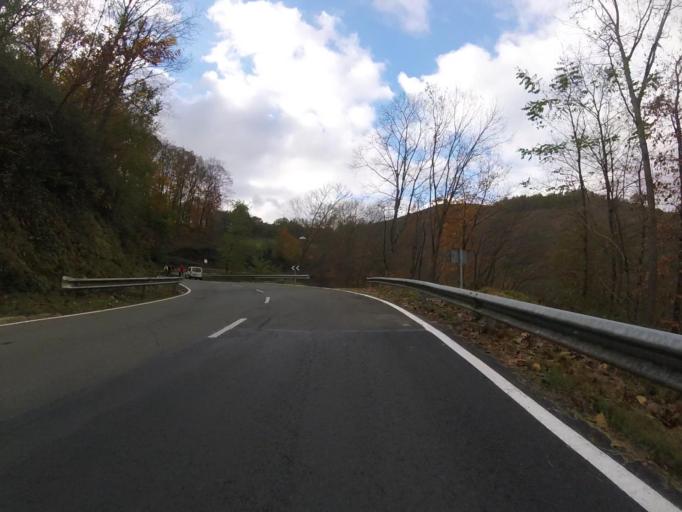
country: ES
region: Navarre
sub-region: Provincia de Navarra
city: Goizueta
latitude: 43.2043
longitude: -1.8569
